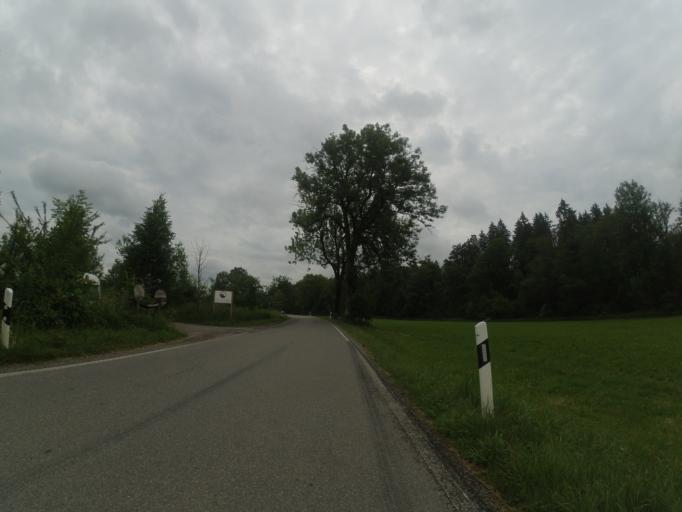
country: DE
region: Bavaria
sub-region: Swabia
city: Heimenkirch
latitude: 47.6790
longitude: 9.8893
